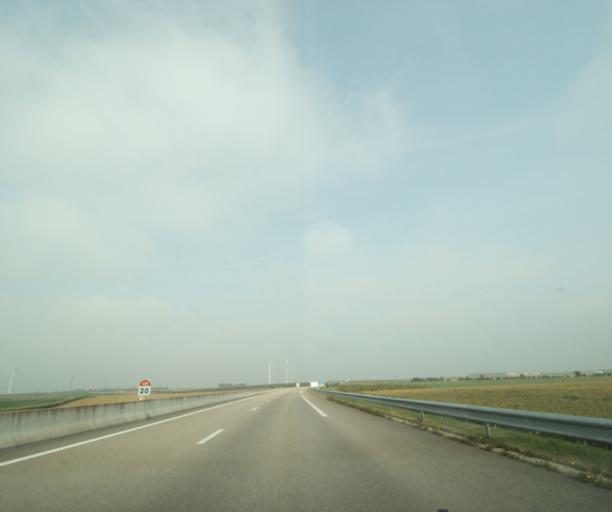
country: FR
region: Lower Normandy
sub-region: Departement de l'Orne
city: Argentan
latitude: 48.7047
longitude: -0.0467
